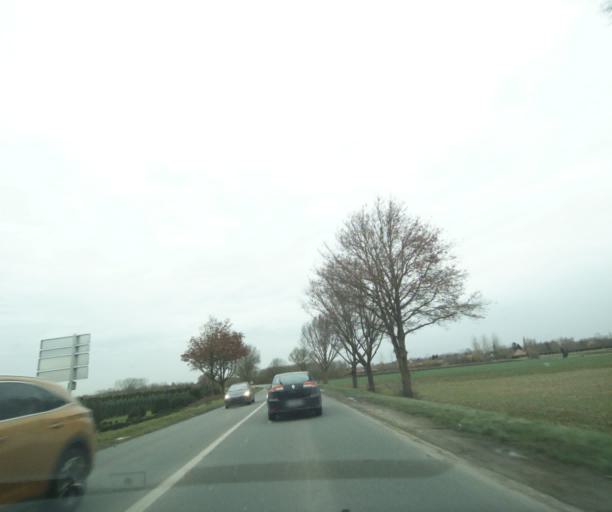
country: FR
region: Nord-Pas-de-Calais
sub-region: Departement du Nord
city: Vicq
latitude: 50.4061
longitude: 3.6154
